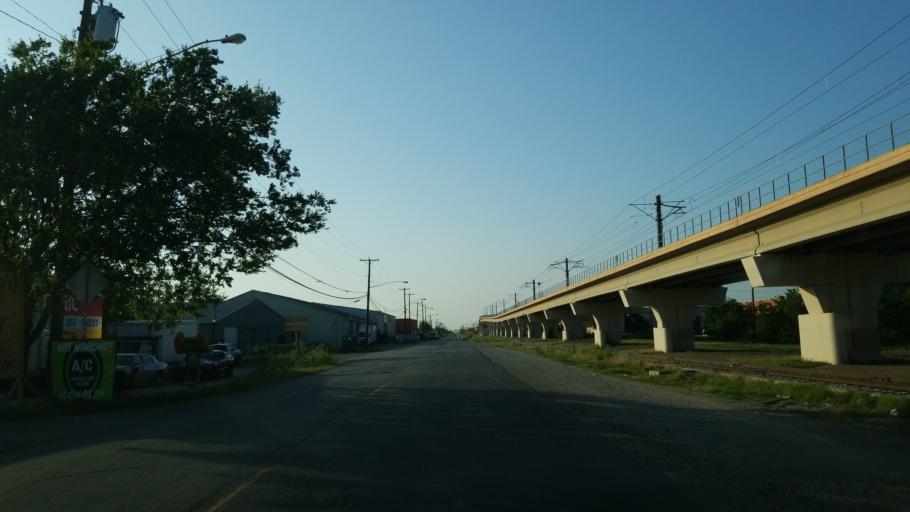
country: US
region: Texas
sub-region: Dallas County
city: Farmers Branch
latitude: 32.8752
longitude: -96.8820
